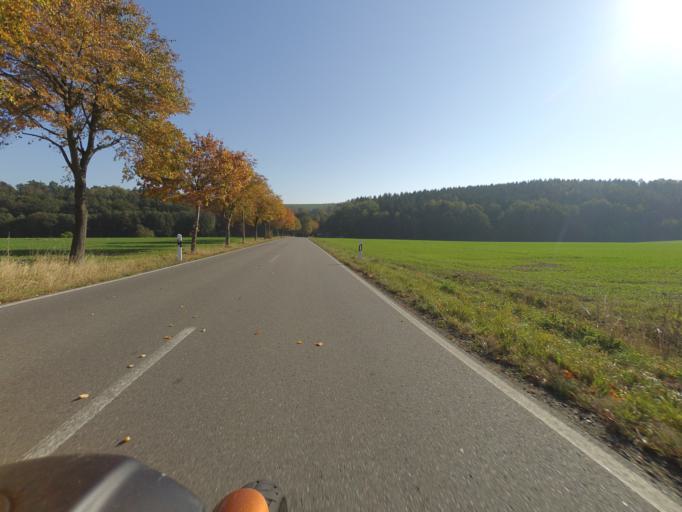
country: DE
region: Saxony
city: Rabenau
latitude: 50.9336
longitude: 13.6139
